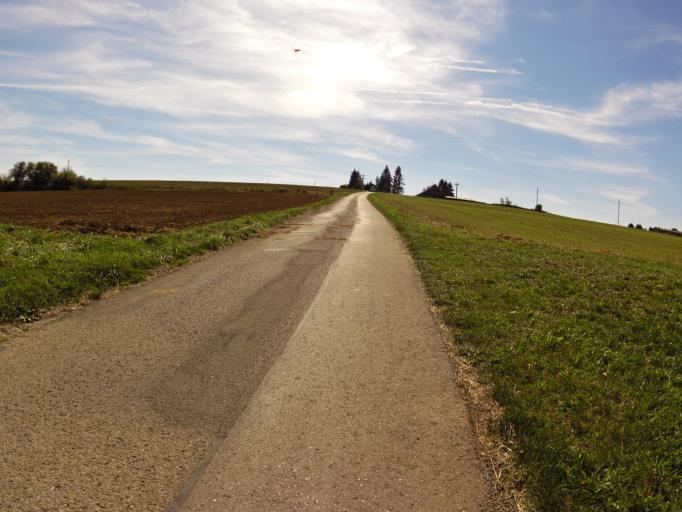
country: DE
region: Baden-Wuerttemberg
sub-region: Freiburg Region
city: Donaueschingen
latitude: 47.9710
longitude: 8.4970
